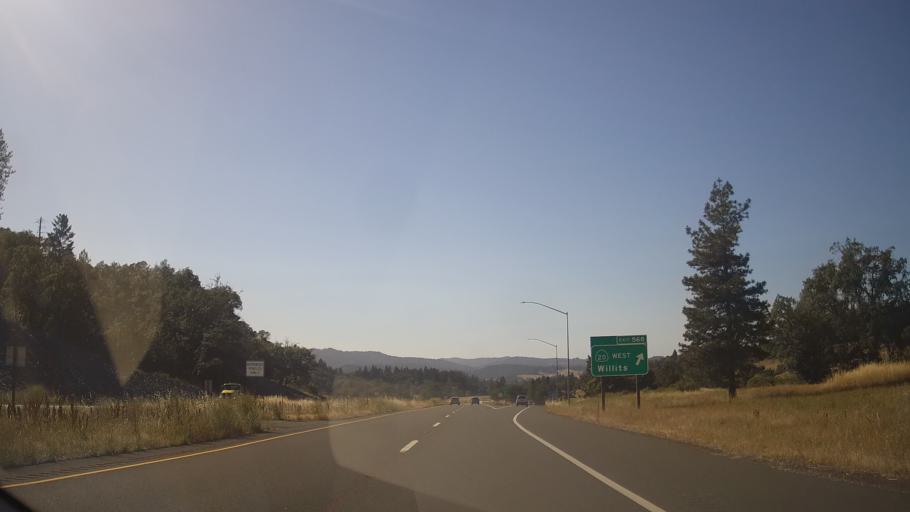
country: US
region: California
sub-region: Mendocino County
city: Willits
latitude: 39.3715
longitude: -123.3208
